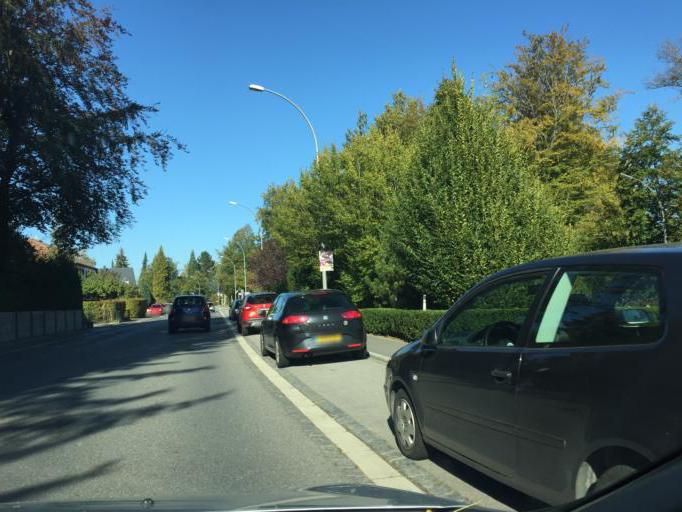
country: LU
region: Luxembourg
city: Bridel
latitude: 49.6514
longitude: 6.0828
